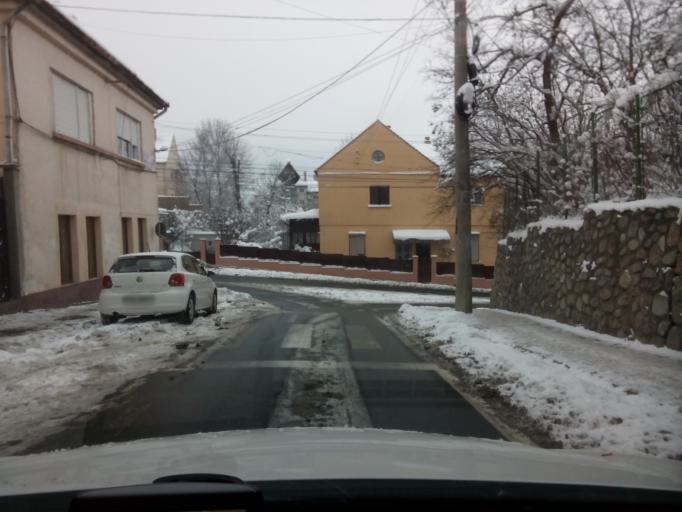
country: RO
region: Sibiu
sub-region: Municipiul Sibiu
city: Sibiu
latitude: 45.7900
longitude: 24.1408
